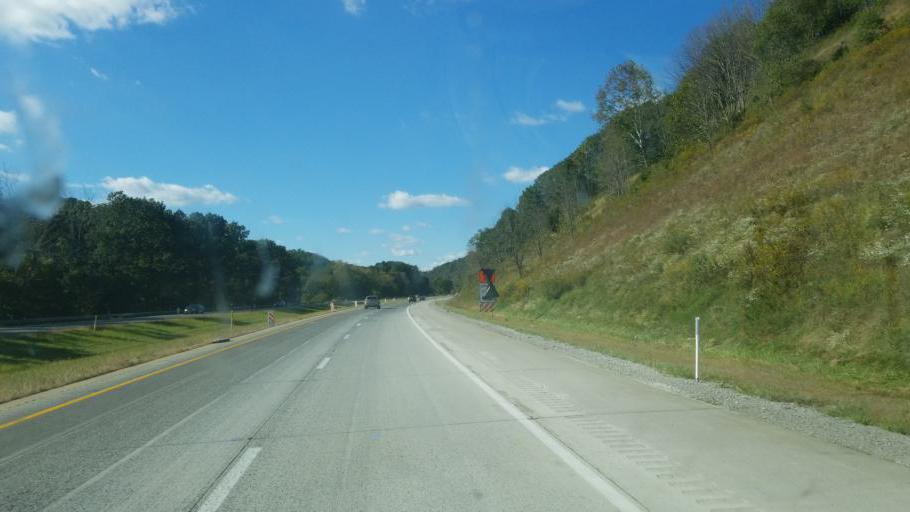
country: US
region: West Virginia
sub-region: Monongalia County
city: Star City
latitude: 39.7497
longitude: -80.0743
